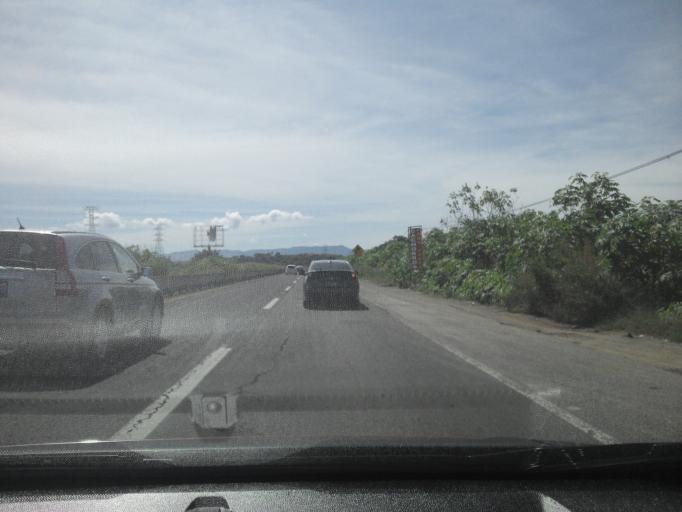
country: MX
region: Jalisco
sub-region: Tala
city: Los Ruisenores
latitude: 20.6859
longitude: -103.6938
